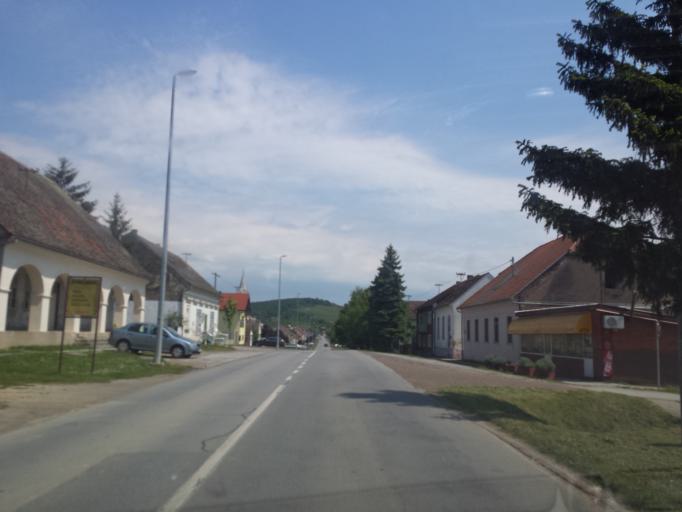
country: HR
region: Brodsko-Posavska
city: Oriovac
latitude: 45.1646
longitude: 17.7925
